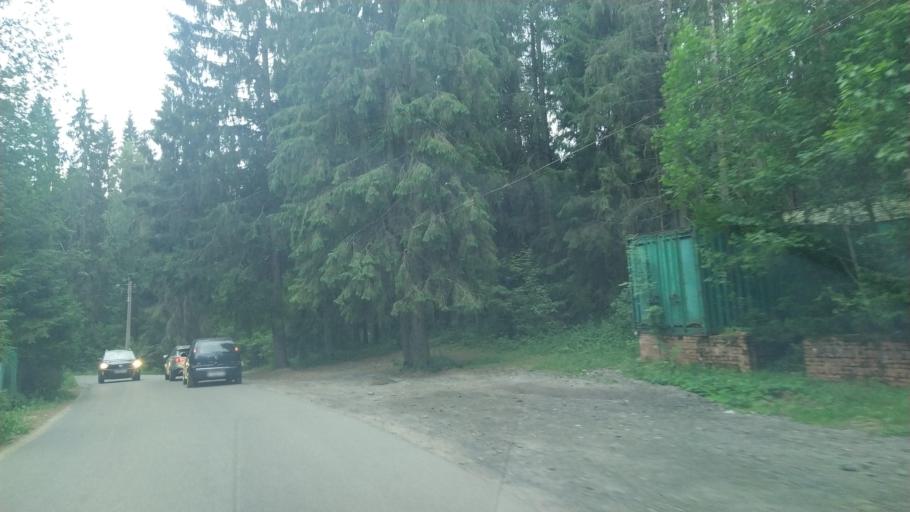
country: RU
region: Leningrad
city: Toksovo
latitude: 60.1687
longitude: 30.5325
